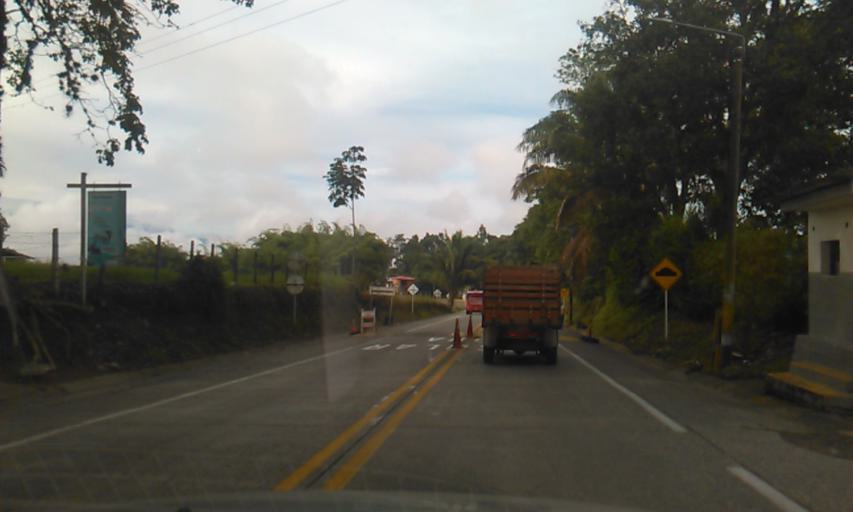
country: CO
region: Quindio
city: Armenia
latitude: 4.4920
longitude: -75.7020
